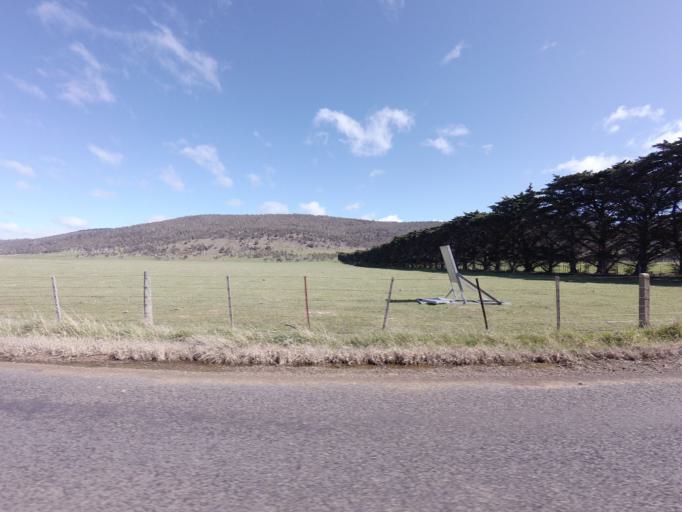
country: AU
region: Tasmania
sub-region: Northern Midlands
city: Evandale
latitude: -41.9664
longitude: 147.4411
